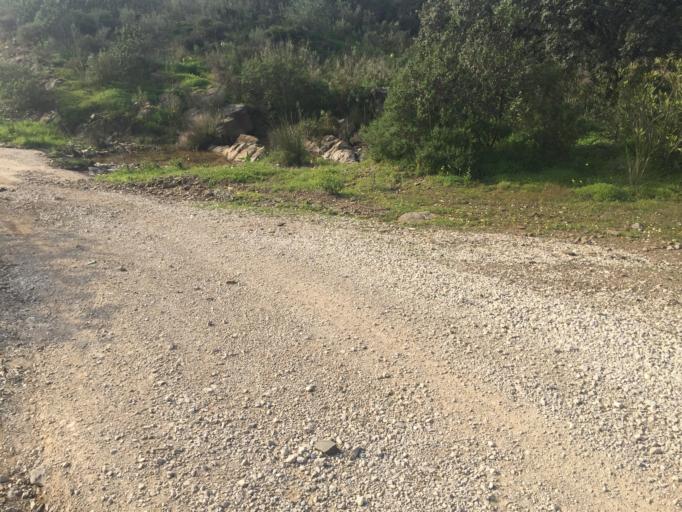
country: PT
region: Faro
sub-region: Castro Marim
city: Castro Marim
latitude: 37.2294
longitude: -7.5553
